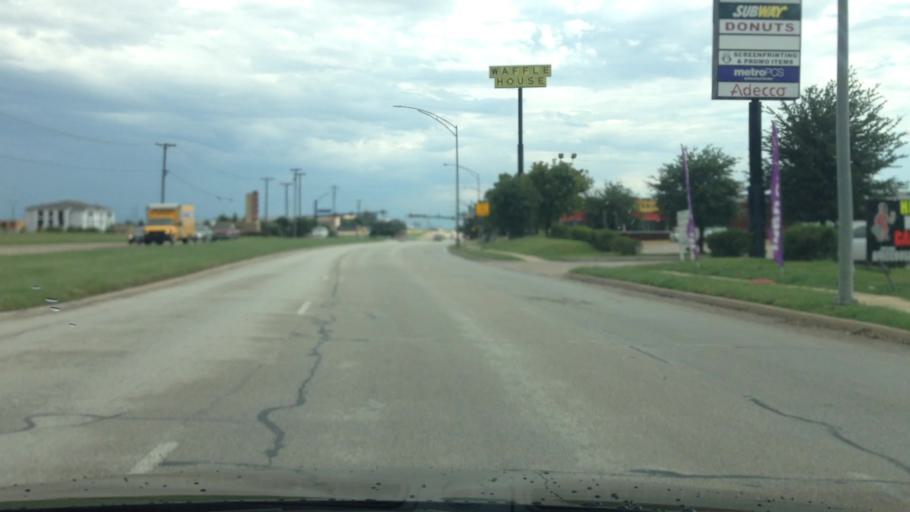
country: US
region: Texas
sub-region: Tarrant County
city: Watauga
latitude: 32.8370
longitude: -97.2907
